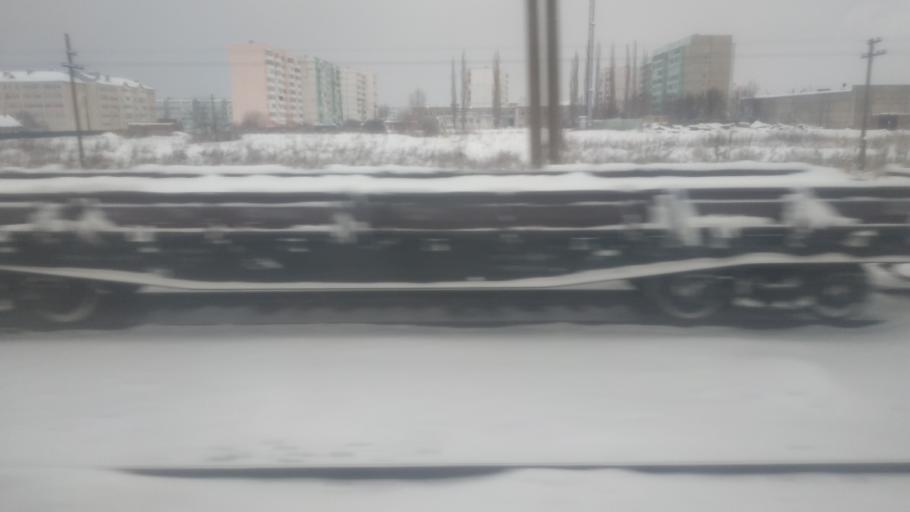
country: RU
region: Bashkortostan
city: Amzya
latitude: 56.2408
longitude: 54.5557
